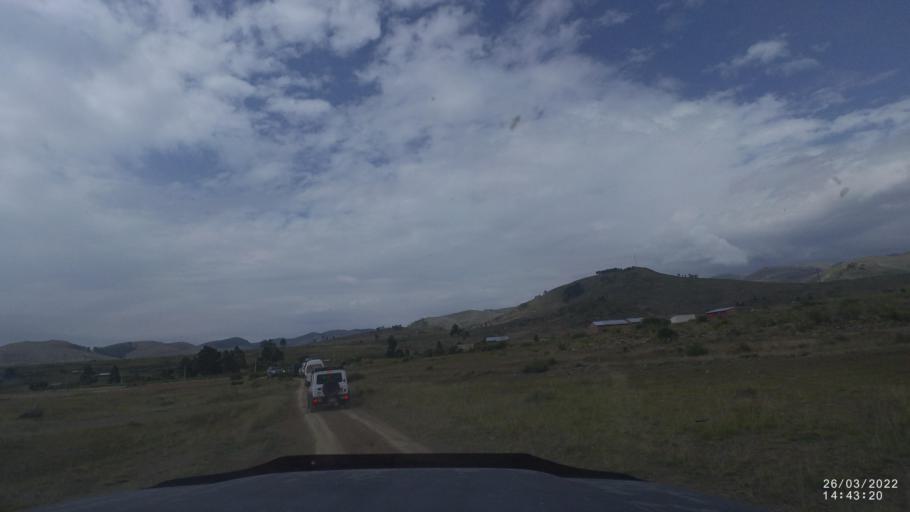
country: BO
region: Cochabamba
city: Cliza
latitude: -17.7380
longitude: -65.8508
